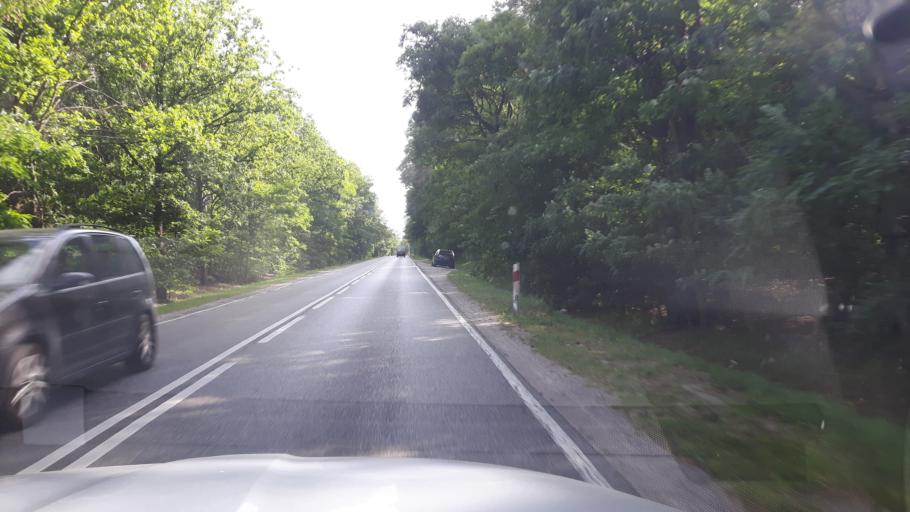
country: PL
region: Masovian Voivodeship
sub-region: Powiat wolominski
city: Radzymin
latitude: 52.3863
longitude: 21.2102
